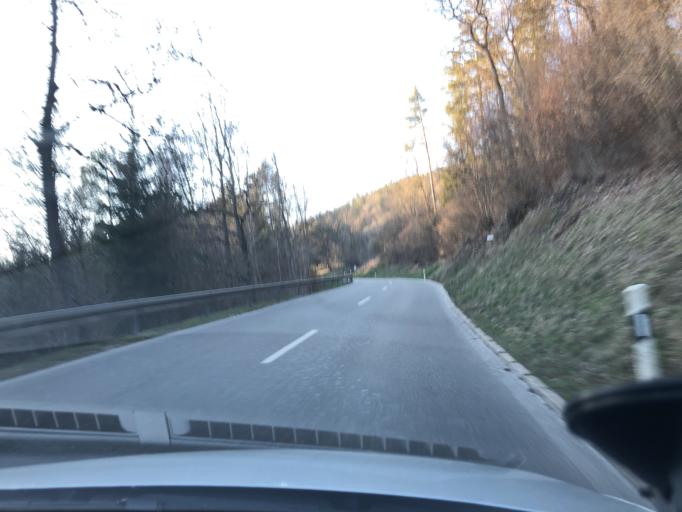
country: DE
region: Baden-Wuerttemberg
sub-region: Freiburg Region
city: Braunlingen
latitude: 47.8513
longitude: 8.4478
